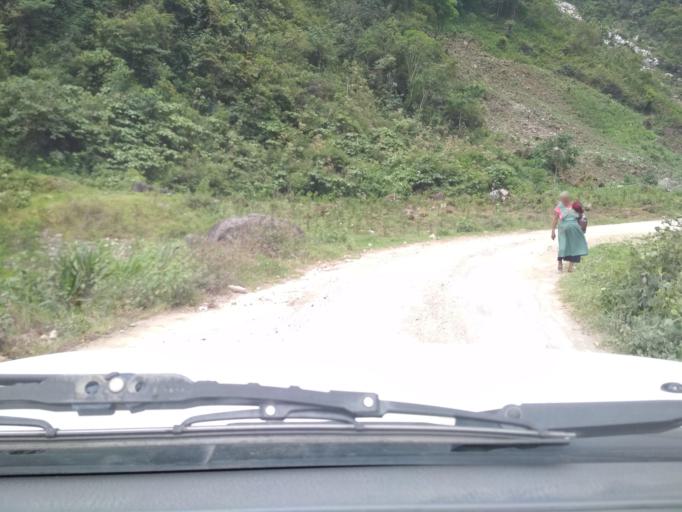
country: MX
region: Veracruz
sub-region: La Perla
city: Metlac Hernandez (Metlac Primero)
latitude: 18.9840
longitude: -97.1319
